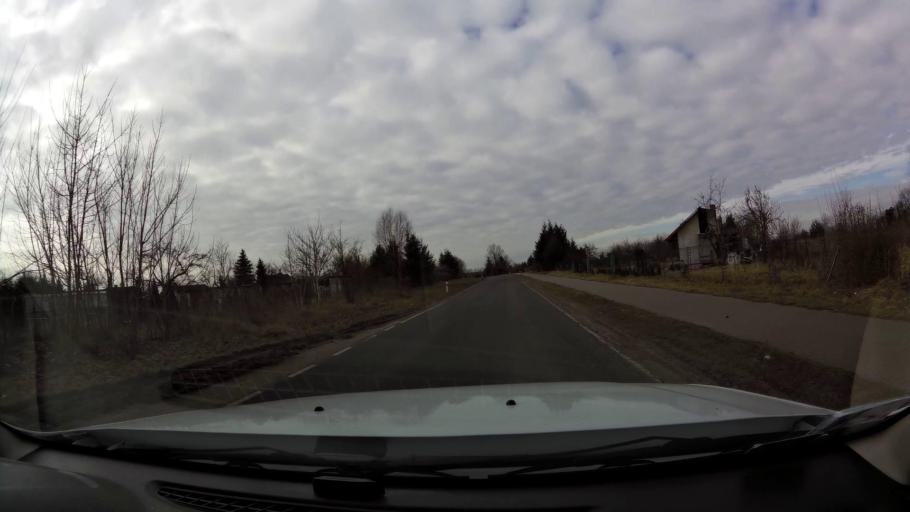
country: PL
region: West Pomeranian Voivodeship
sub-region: Powiat mysliborski
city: Debno
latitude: 52.7318
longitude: 14.6927
